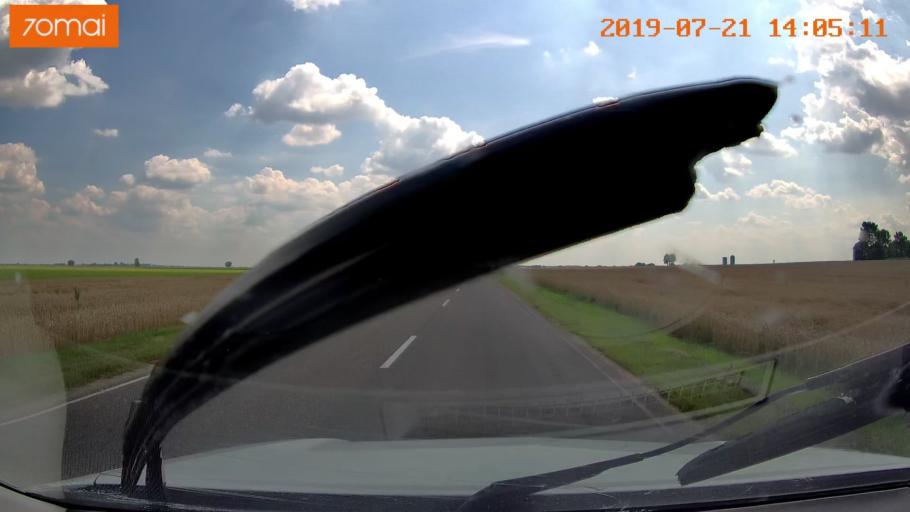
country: BY
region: Grodnenskaya
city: Lyubcha
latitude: 53.7148
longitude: 26.1018
